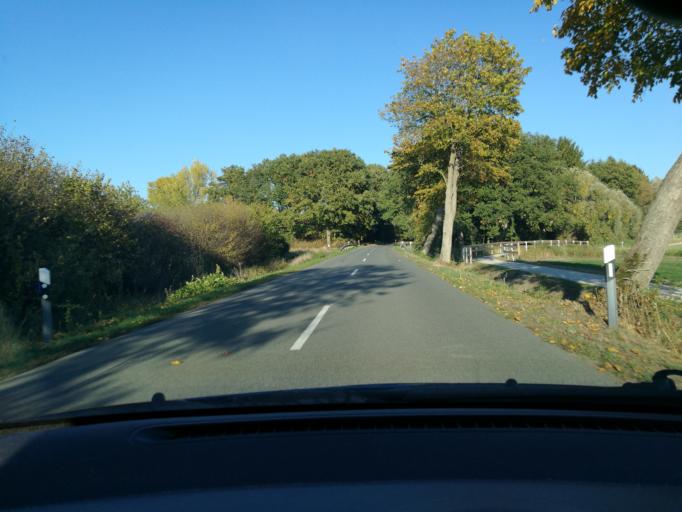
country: DE
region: Lower Saxony
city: Ludersburg
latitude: 53.3274
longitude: 10.5847
